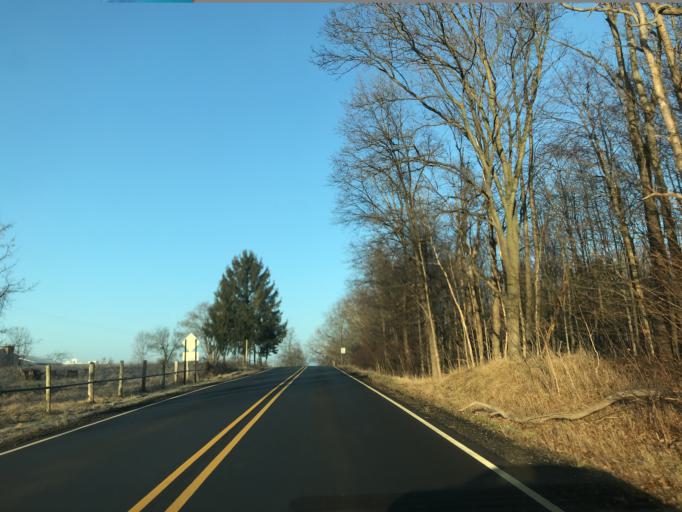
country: US
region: Michigan
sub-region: Ingham County
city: Leslie
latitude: 42.4366
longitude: -84.5422
